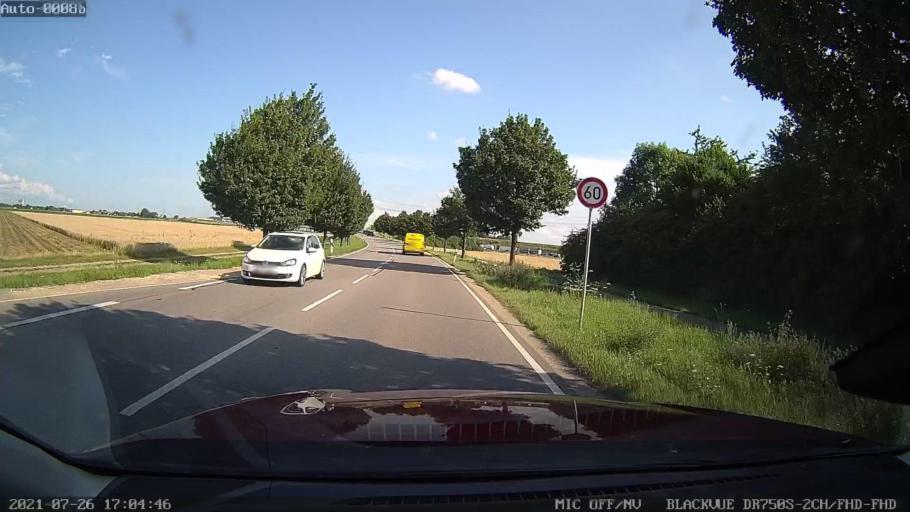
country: DE
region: Bavaria
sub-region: Upper Palatinate
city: Barbing
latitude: 48.9977
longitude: 12.2093
